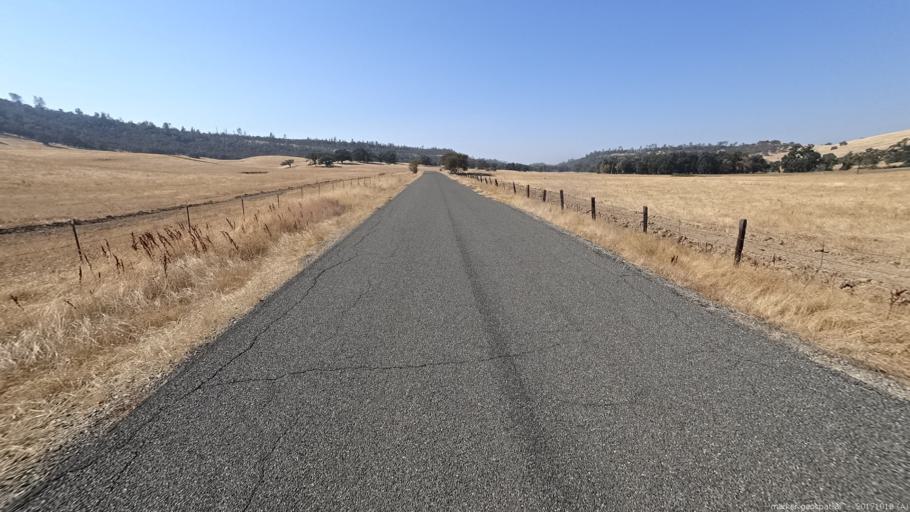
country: US
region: California
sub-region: Shasta County
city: Palo Cedro
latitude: 40.5464
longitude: -122.0819
